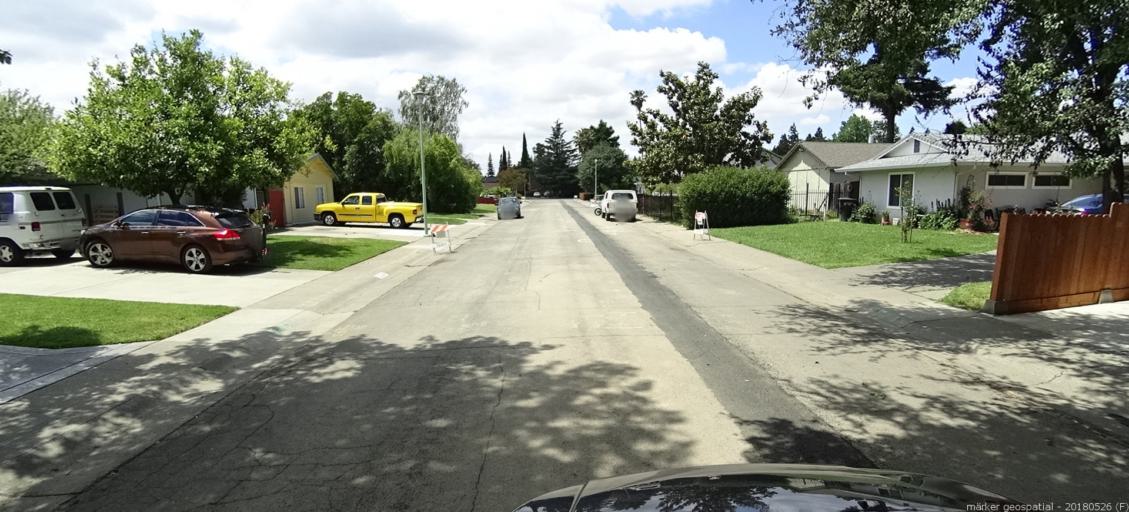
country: US
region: California
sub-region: Sacramento County
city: Sacramento
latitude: 38.6121
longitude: -121.4889
